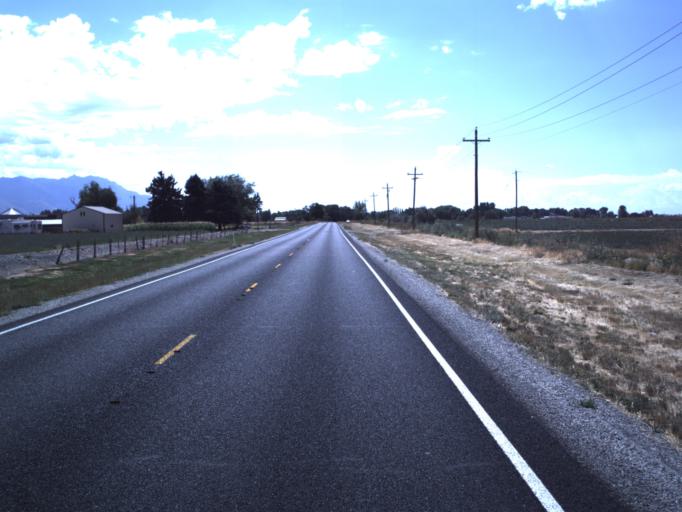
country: US
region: Utah
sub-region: Box Elder County
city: Honeyville
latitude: 41.6333
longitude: -112.1280
